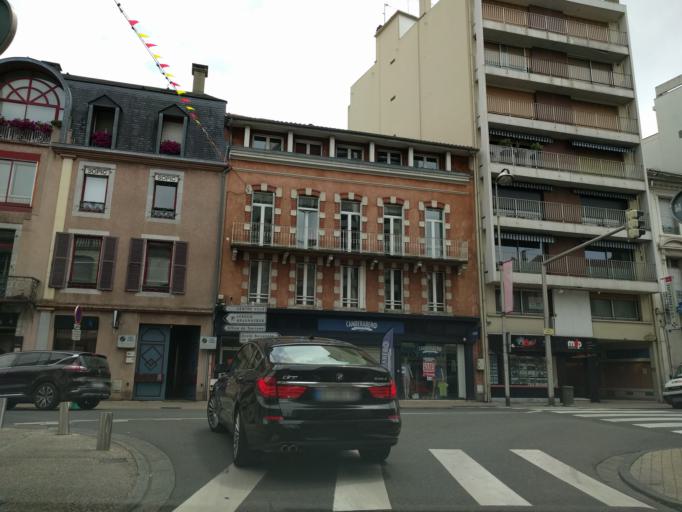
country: FR
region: Midi-Pyrenees
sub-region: Departement des Hautes-Pyrenees
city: Tarbes
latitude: 43.2317
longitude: 0.0734
